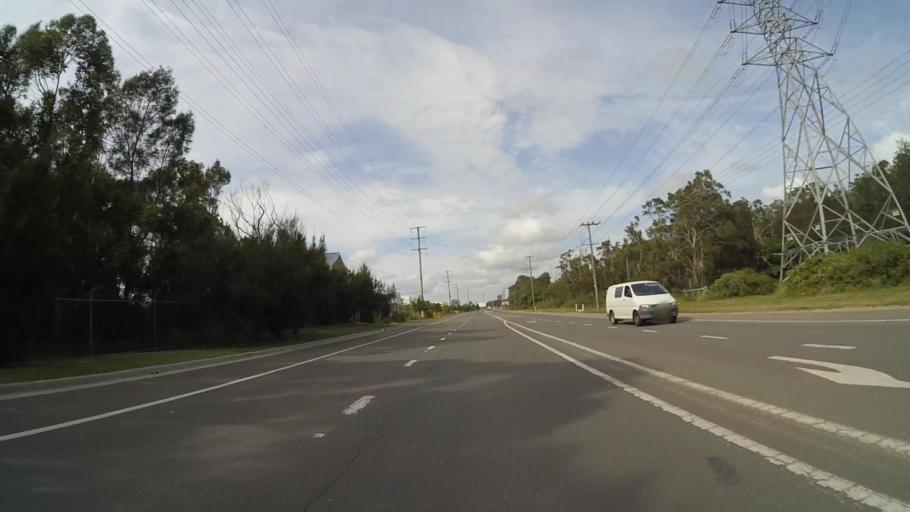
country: AU
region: New South Wales
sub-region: Sutherland Shire
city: Cronulla
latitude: -34.0331
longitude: 151.1622
